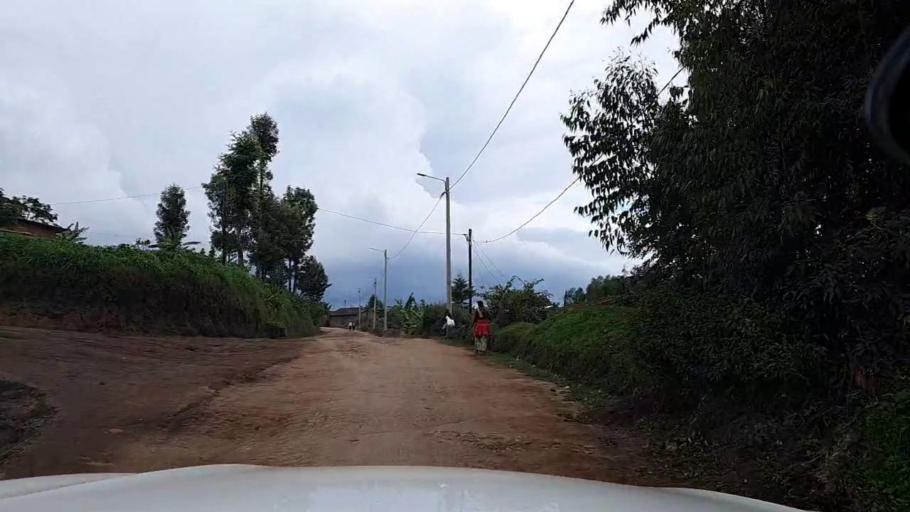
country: BI
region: Kayanza
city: Kayanza
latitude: -2.7996
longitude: 29.5052
